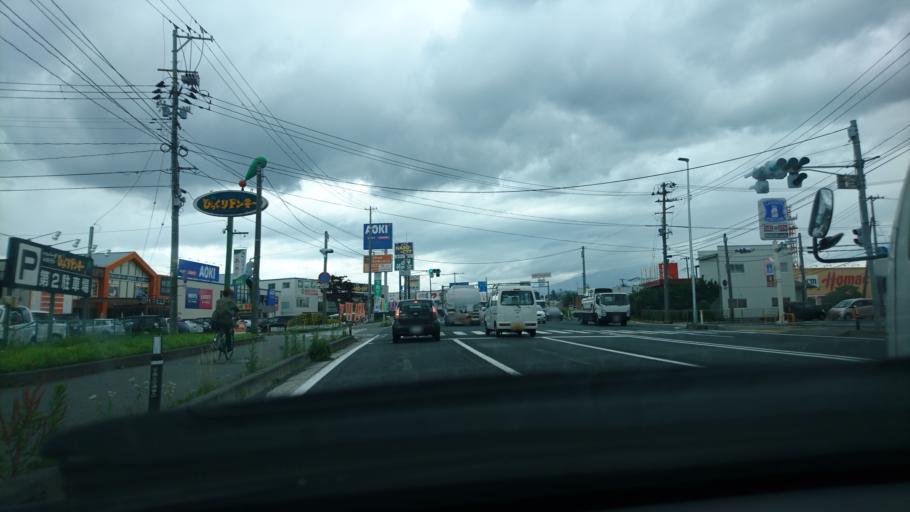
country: JP
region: Iwate
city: Morioka-shi
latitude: 39.7252
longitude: 141.1254
